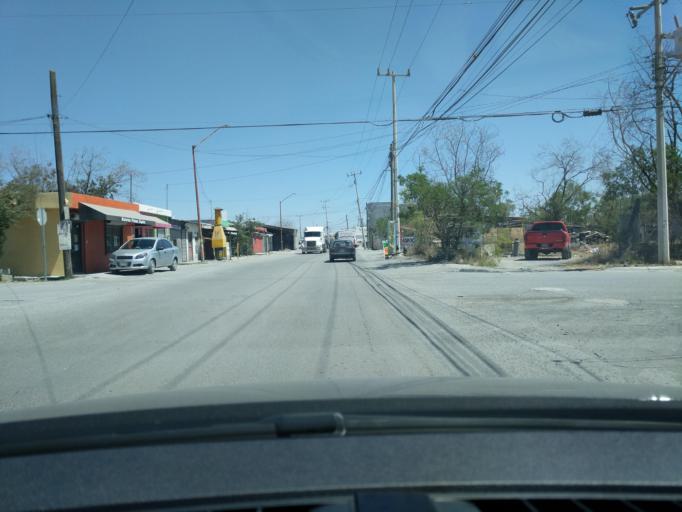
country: MX
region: Nuevo Leon
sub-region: Salinas Victoria
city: Emiliano Zapata
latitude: 25.9092
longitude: -100.2725
